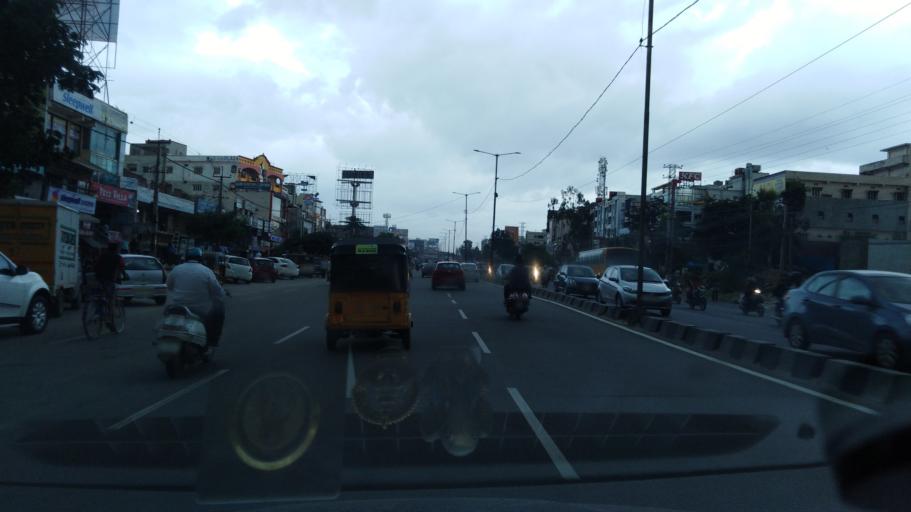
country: IN
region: Telangana
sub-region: Medak
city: Serilingampalle
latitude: 17.4950
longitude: 78.3546
